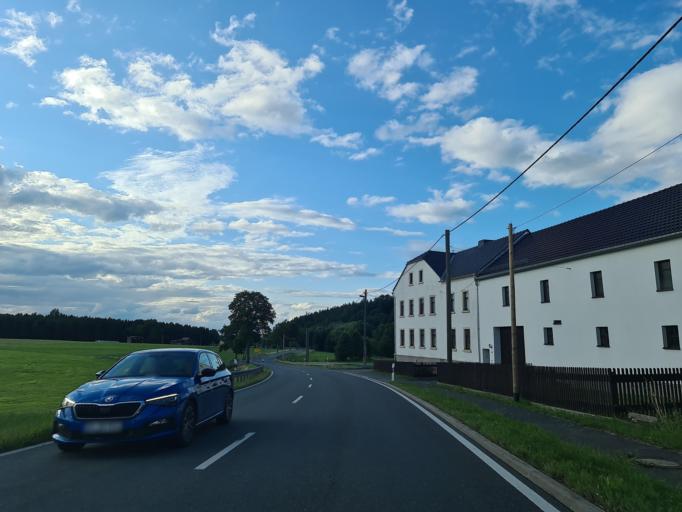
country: DE
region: Saxony
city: Mehltheuer
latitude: 50.5505
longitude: 12.0126
